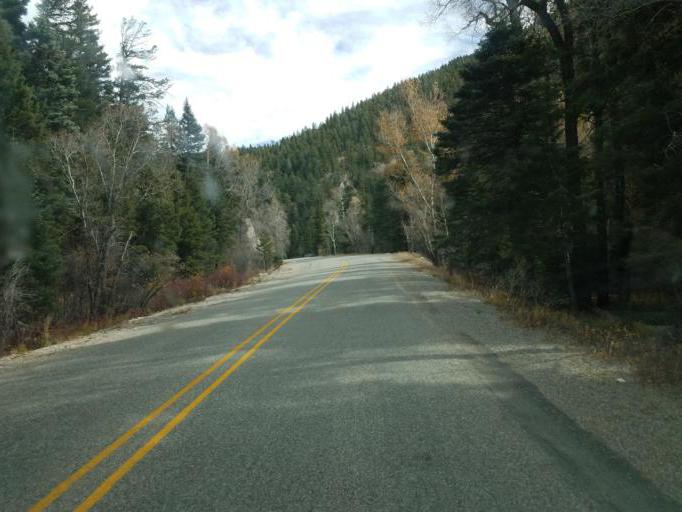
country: US
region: New Mexico
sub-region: Taos County
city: Arroyo Seco
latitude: 36.5692
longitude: -105.5204
